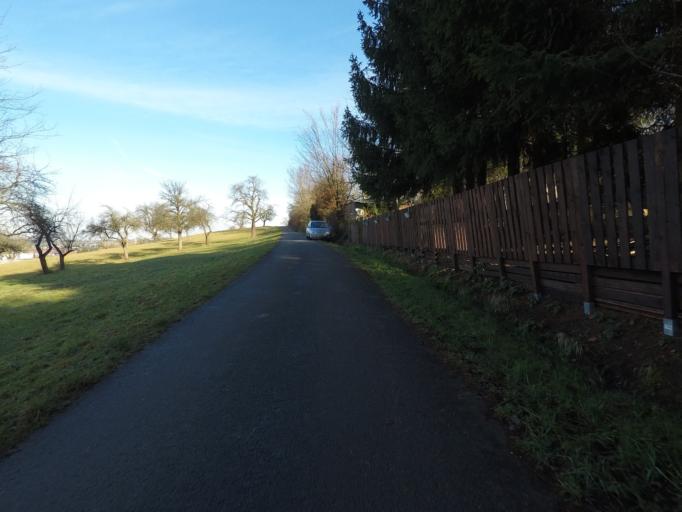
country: DE
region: Baden-Wuerttemberg
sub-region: Tuebingen Region
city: Wannweil
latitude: 48.4901
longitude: 9.1631
